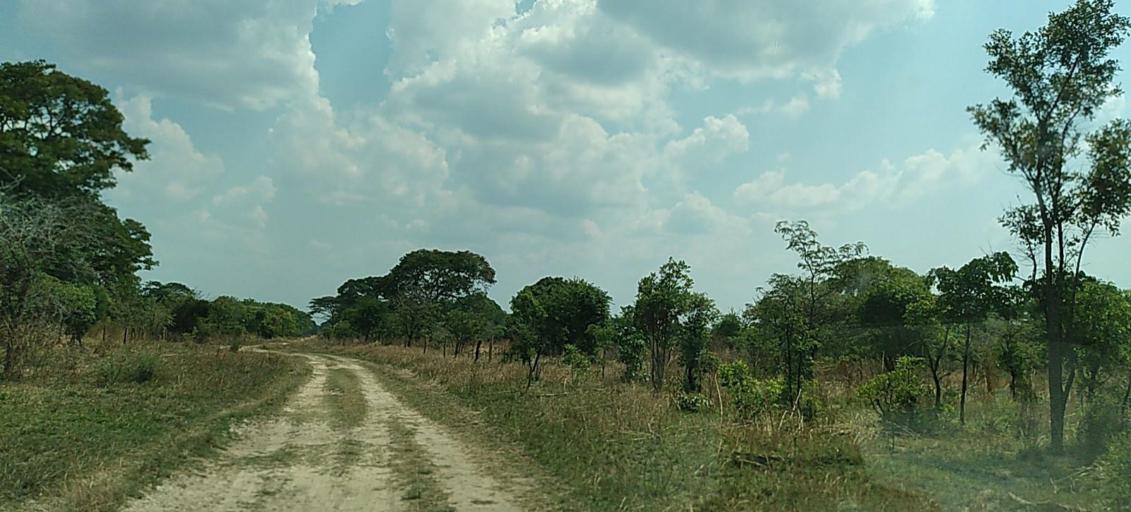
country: ZM
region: Copperbelt
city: Mpongwe
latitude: -13.8328
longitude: 27.9390
